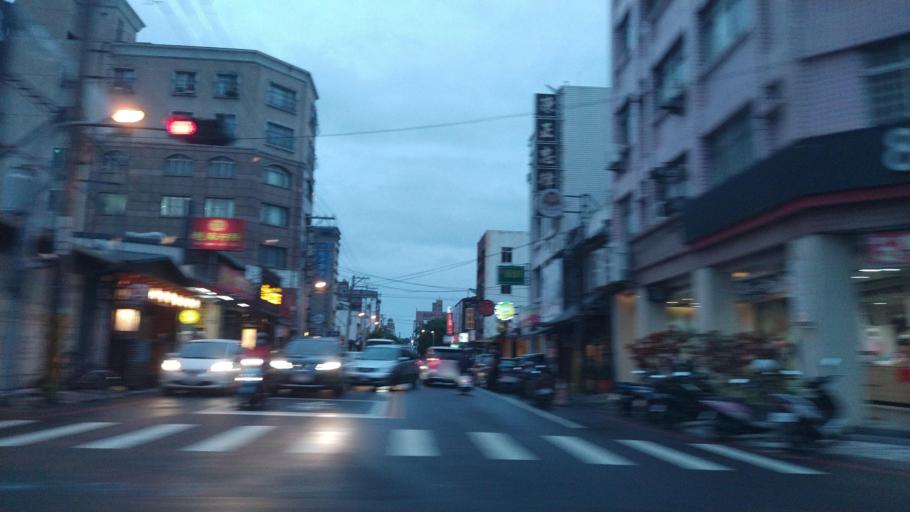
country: TW
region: Taiwan
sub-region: Hualien
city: Hualian
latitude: 23.9762
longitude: 121.6018
